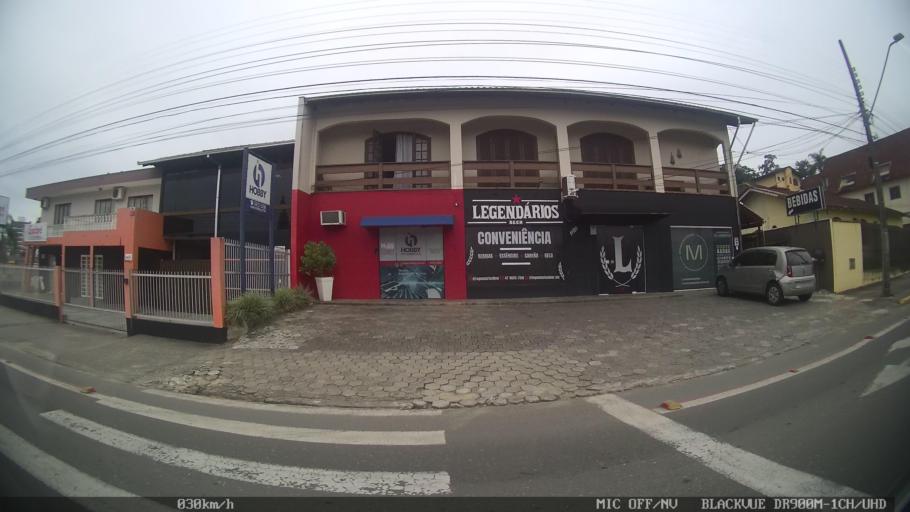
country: BR
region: Santa Catarina
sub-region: Joinville
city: Joinville
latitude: -26.2764
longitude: -48.8323
